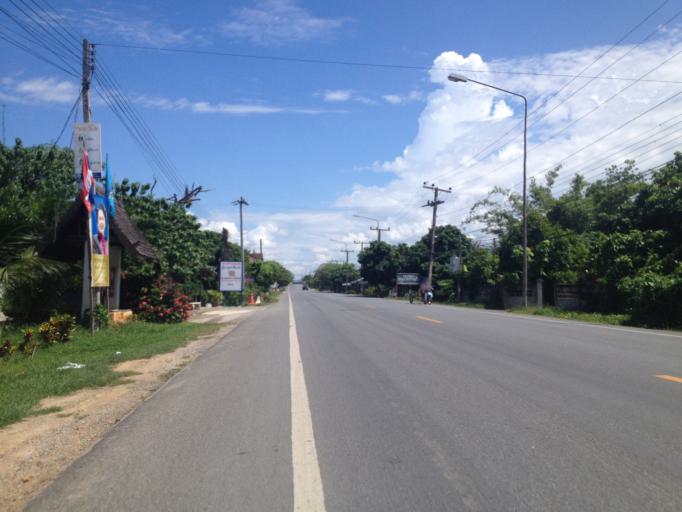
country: TH
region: Lamphun
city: Lamphun
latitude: 18.6016
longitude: 98.9622
